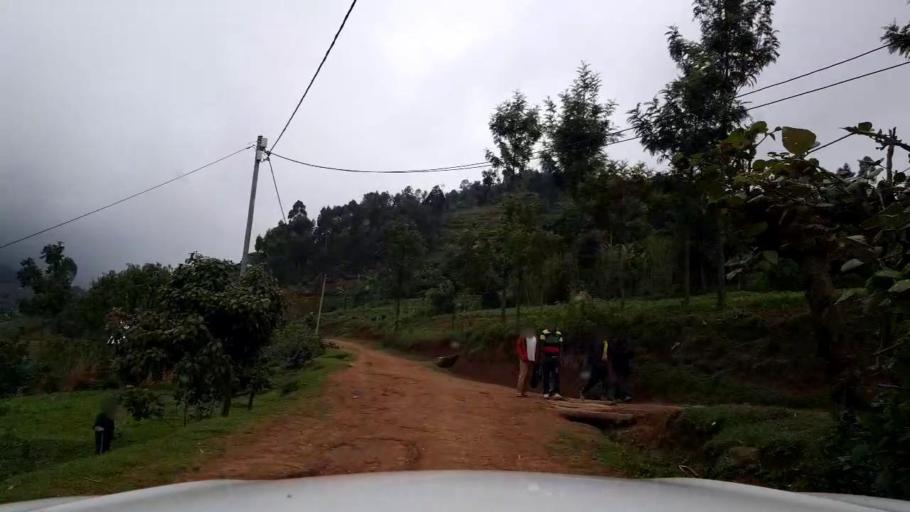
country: RW
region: Northern Province
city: Musanze
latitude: -1.5927
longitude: 29.7856
